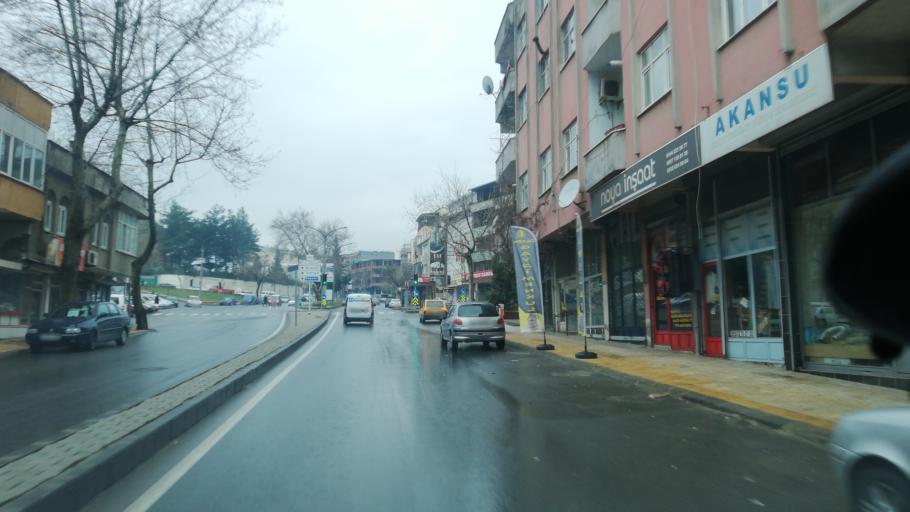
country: TR
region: Kahramanmaras
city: Kahramanmaras
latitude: 37.5887
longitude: 36.9145
